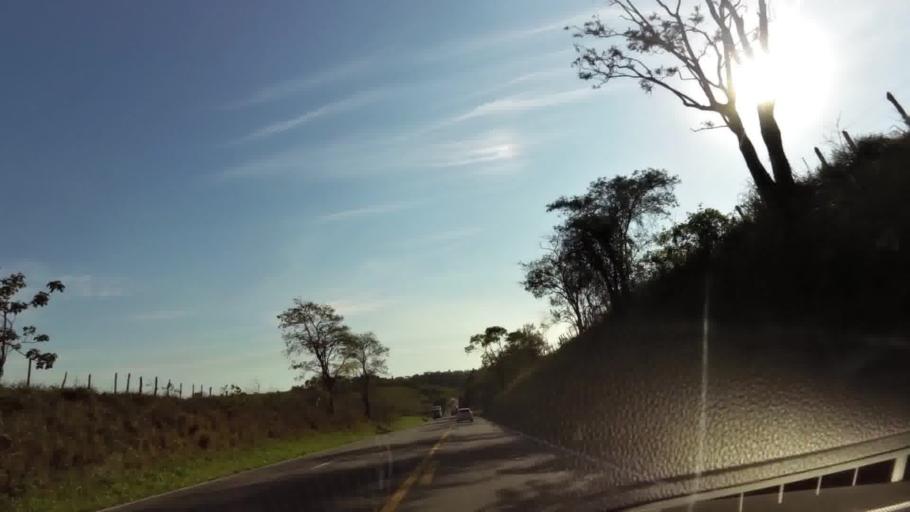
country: BR
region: Espirito Santo
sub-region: Viana
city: Viana
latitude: -20.4826
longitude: -40.4747
